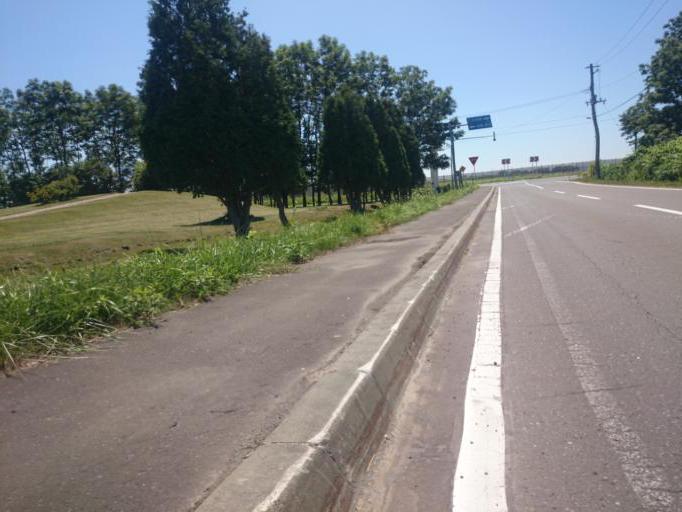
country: JP
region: Hokkaido
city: Ebetsu
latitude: 43.0696
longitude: 141.5962
